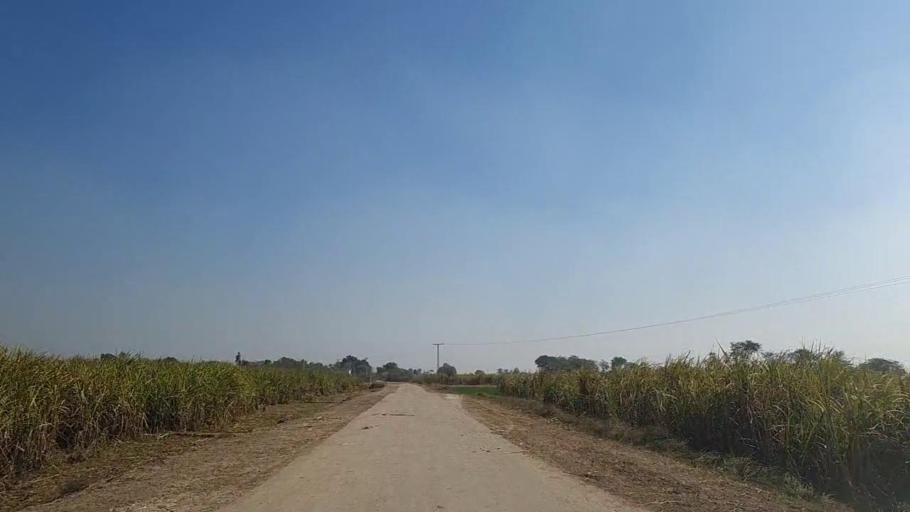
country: PK
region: Sindh
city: Daur
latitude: 26.4822
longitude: 68.3255
